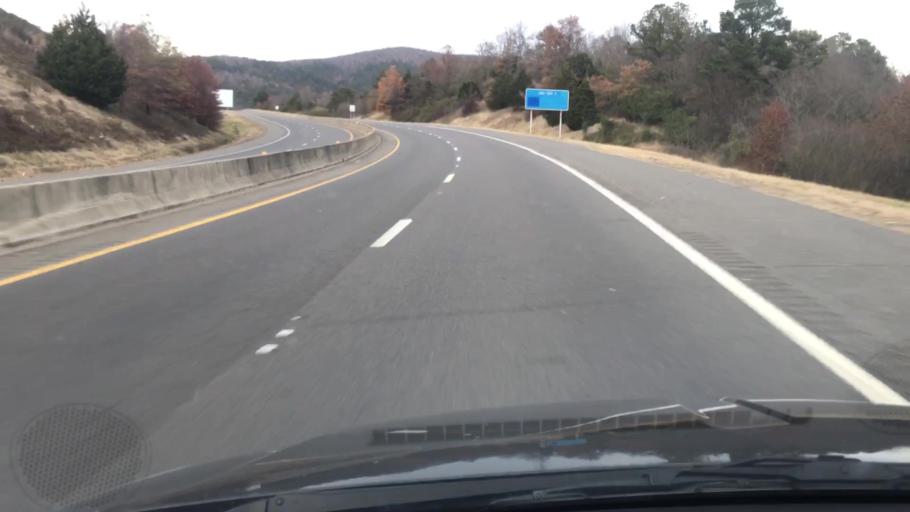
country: US
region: Arkansas
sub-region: Garland County
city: Piney
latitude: 34.4842
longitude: -93.1125
